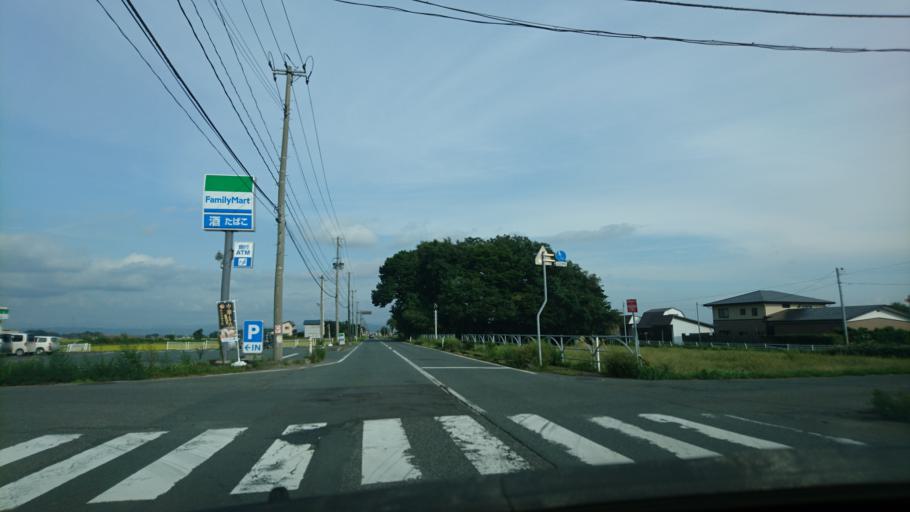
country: JP
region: Iwate
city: Kitakami
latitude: 39.3058
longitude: 141.0065
